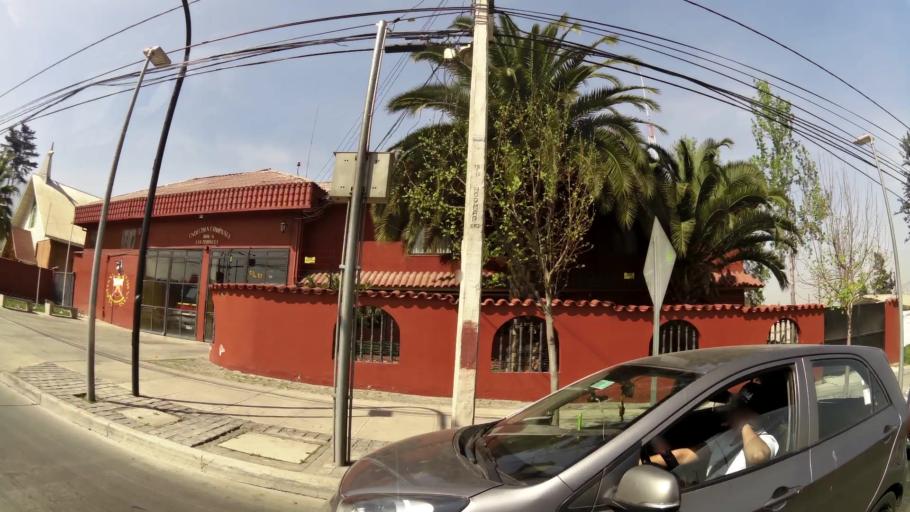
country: CL
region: Santiago Metropolitan
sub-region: Provincia de Santiago
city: Villa Presidente Frei, Nunoa, Santiago, Chile
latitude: -33.5116
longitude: -70.5649
